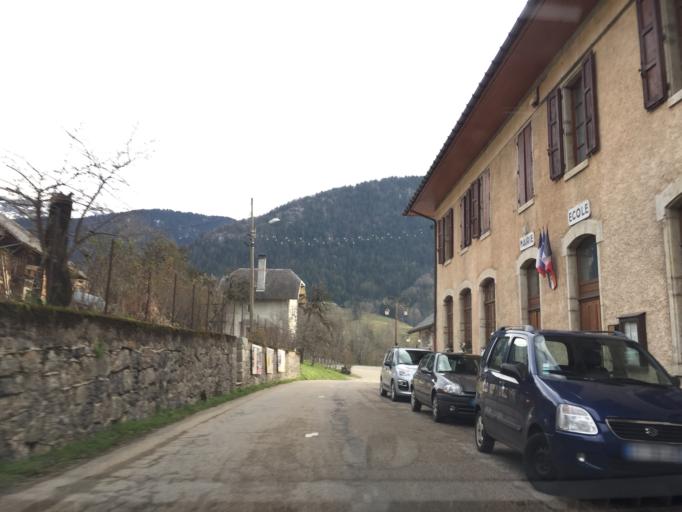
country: FR
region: Rhone-Alpes
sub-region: Departement de la Haute-Savoie
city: Doussard
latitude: 45.7377
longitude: 6.1423
